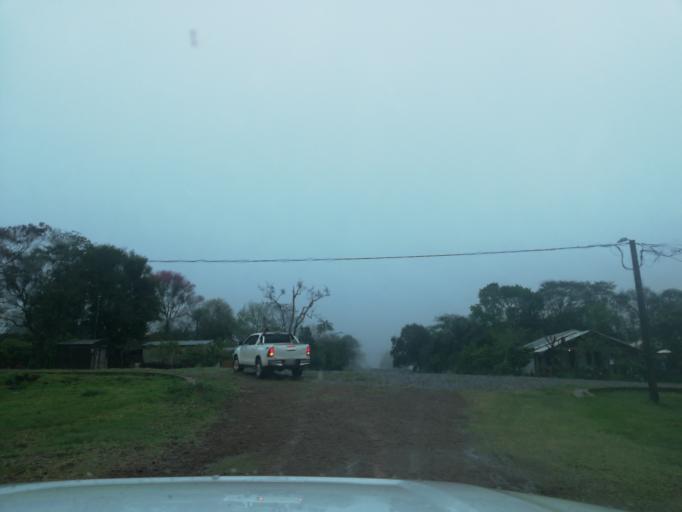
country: AR
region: Misiones
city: Almafuerte
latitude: -27.5075
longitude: -55.4014
